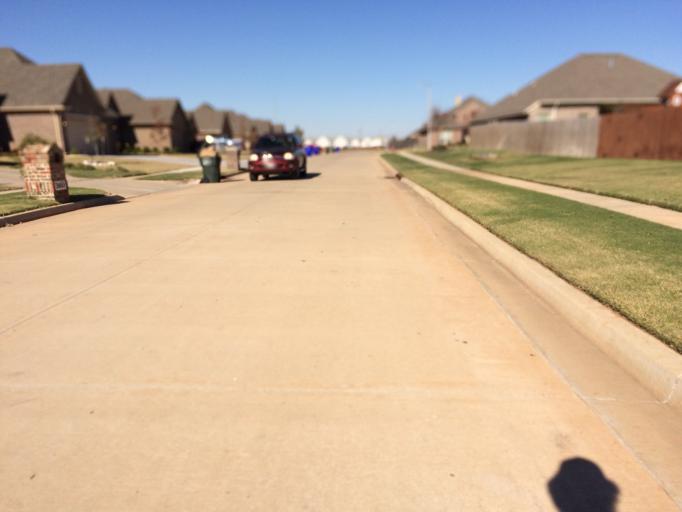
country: US
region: Oklahoma
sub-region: Cleveland County
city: Noble
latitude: 35.1721
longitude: -97.4220
